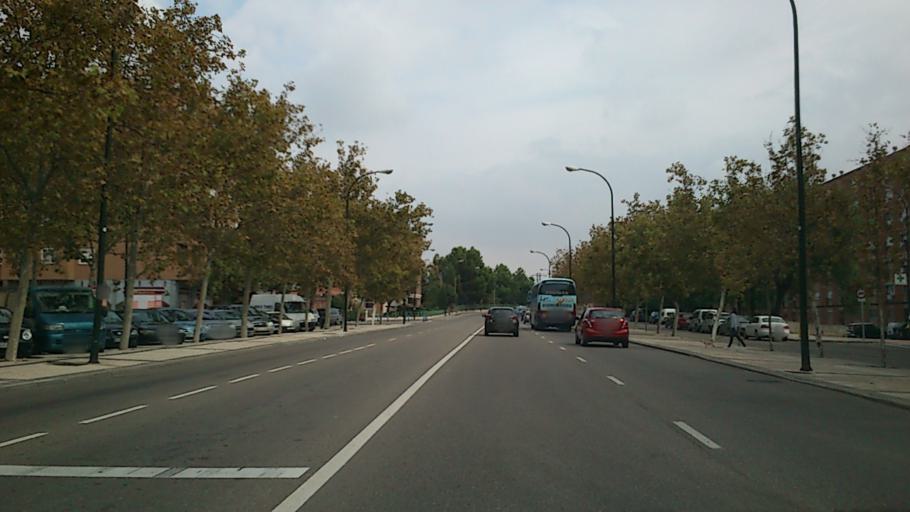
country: ES
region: Aragon
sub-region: Provincia de Zaragoza
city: Zaragoza
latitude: 41.6700
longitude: -0.8460
